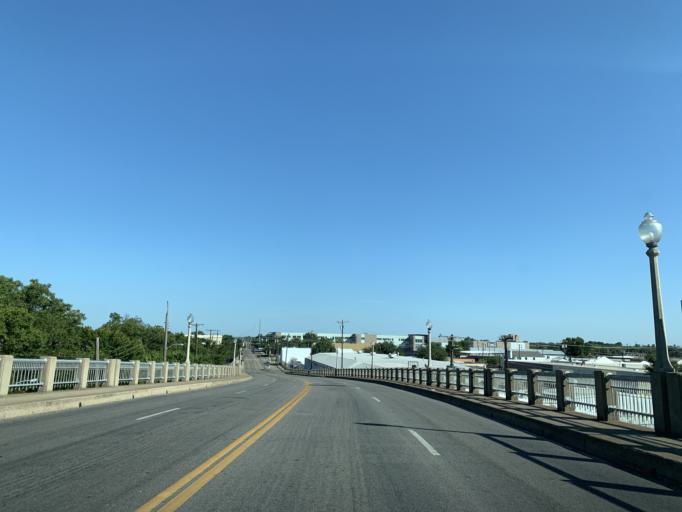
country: US
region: Texas
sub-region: Dallas County
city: Dallas
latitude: 32.7751
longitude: -96.7754
